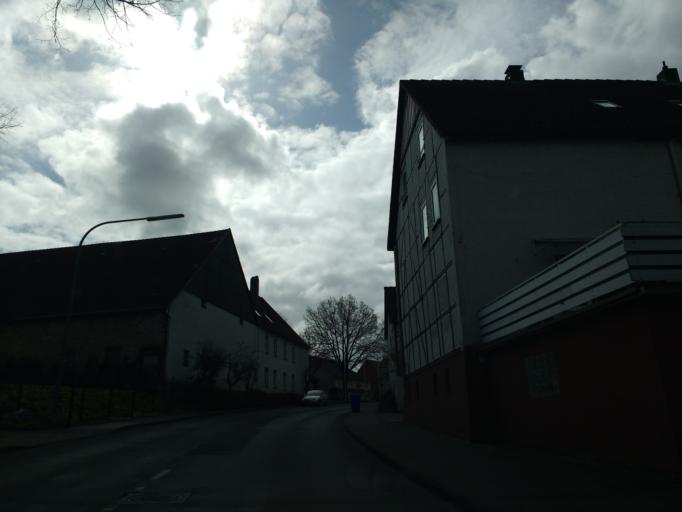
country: DE
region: North Rhine-Westphalia
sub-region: Regierungsbezirk Detmold
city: Wunnenberg
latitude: 51.5167
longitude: 8.7415
